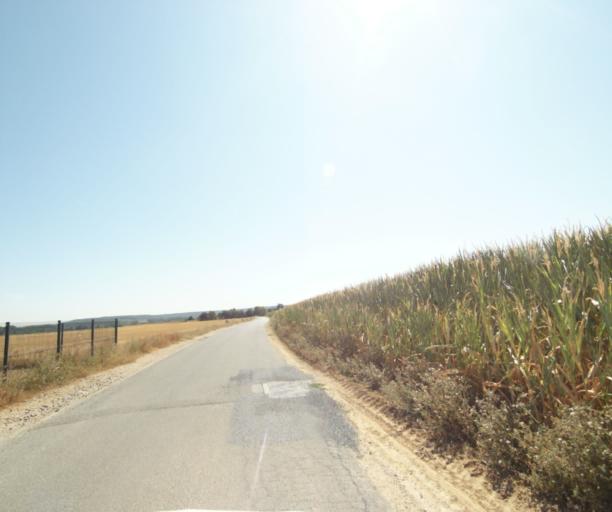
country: FR
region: Ile-de-France
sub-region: Departement de l'Essonne
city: Itteville
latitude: 48.5120
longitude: 2.3478
